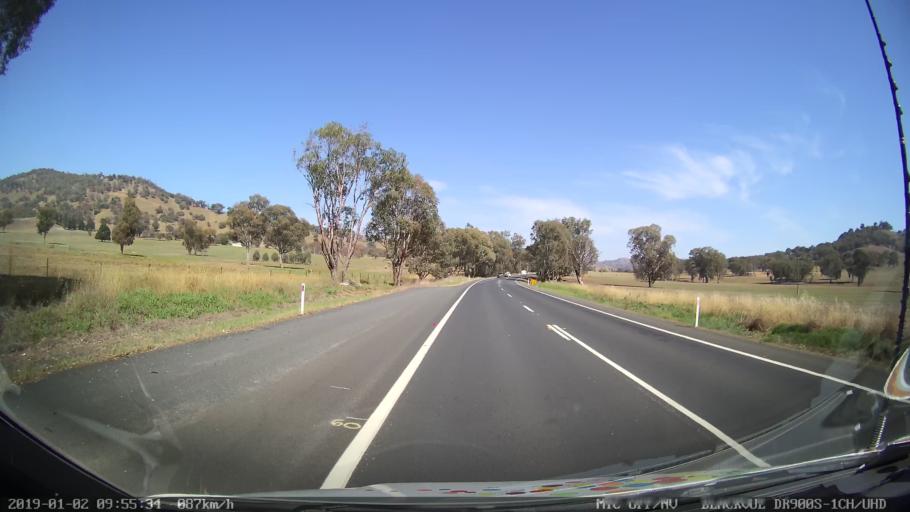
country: AU
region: New South Wales
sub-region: Tumut Shire
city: Tumut
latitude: -35.2225
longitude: 148.1868
